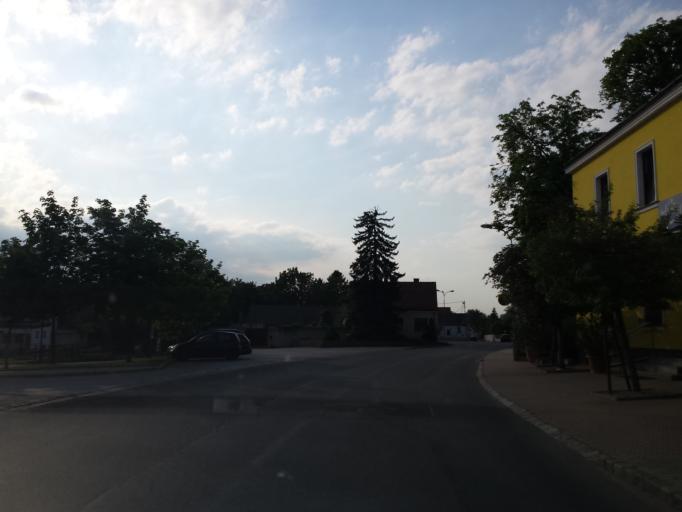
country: AT
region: Lower Austria
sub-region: Politischer Bezirk Ganserndorf
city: Untersiebenbrunn
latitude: 48.2568
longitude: 16.7437
